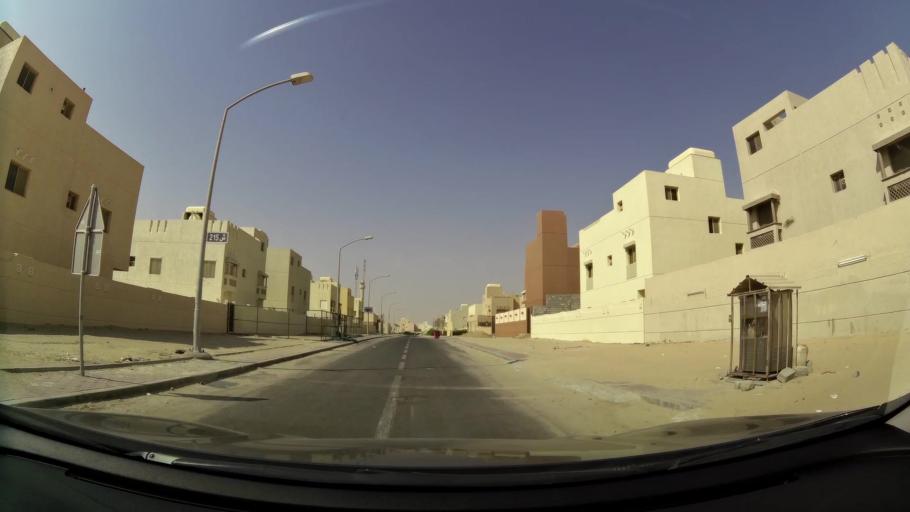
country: KW
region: Al Ahmadi
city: Al Wafrah
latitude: 28.8096
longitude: 48.0606
